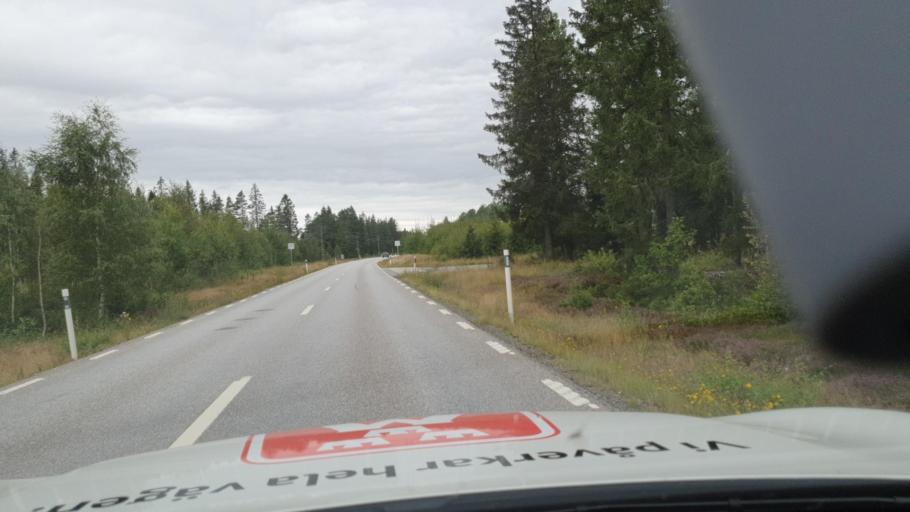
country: SE
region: Vaestra Goetaland
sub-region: Bengtsfors Kommun
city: Billingsfors
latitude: 58.8357
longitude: 12.1223
